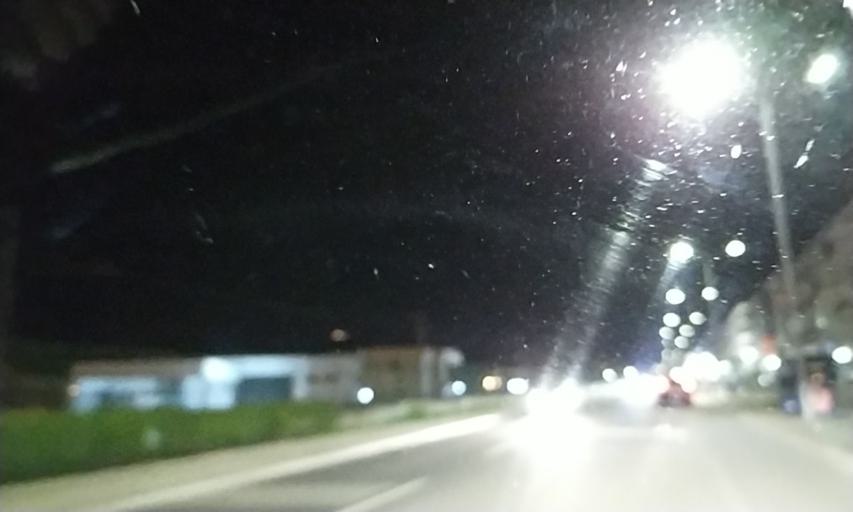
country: PT
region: Castelo Branco
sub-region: Concelho do Fundao
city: Fundao
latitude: 40.1497
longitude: -7.4987
